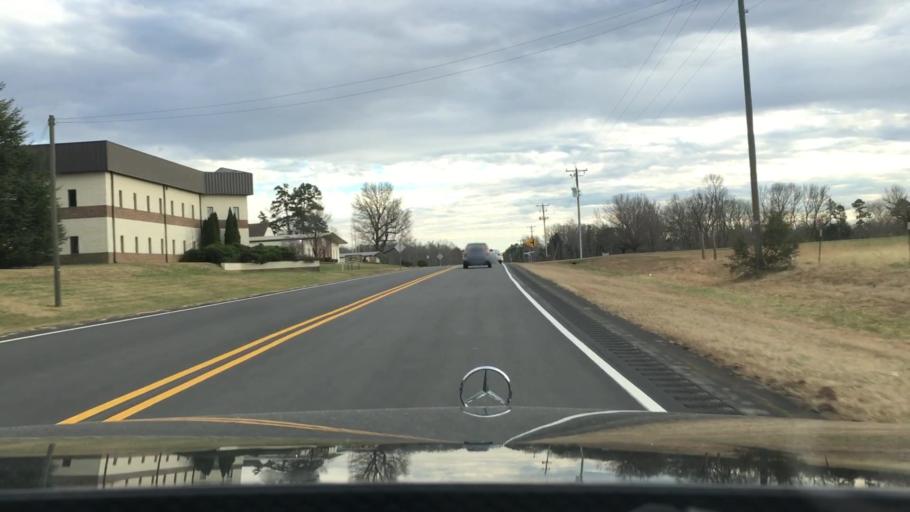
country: US
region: North Carolina
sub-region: Alamance County
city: Mebane
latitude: 36.2690
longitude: -79.1976
